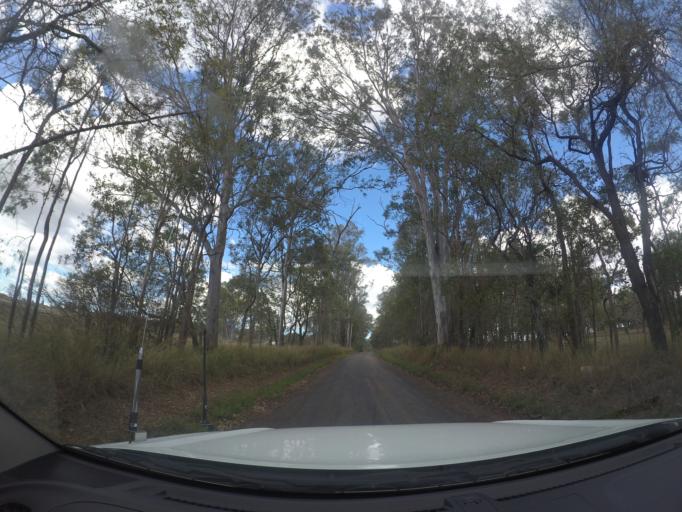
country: AU
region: Queensland
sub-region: Logan
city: Cedar Vale
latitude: -27.8936
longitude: 152.9681
